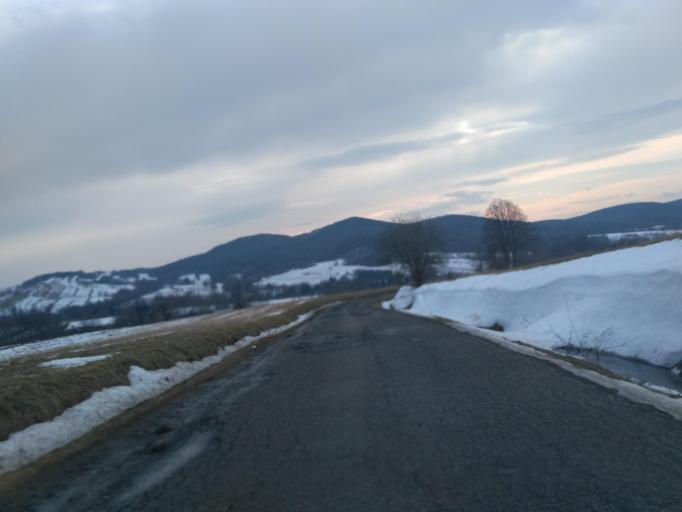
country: PL
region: Subcarpathian Voivodeship
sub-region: Powiat brzozowski
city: Dydnia
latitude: 49.6394
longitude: 22.1640
